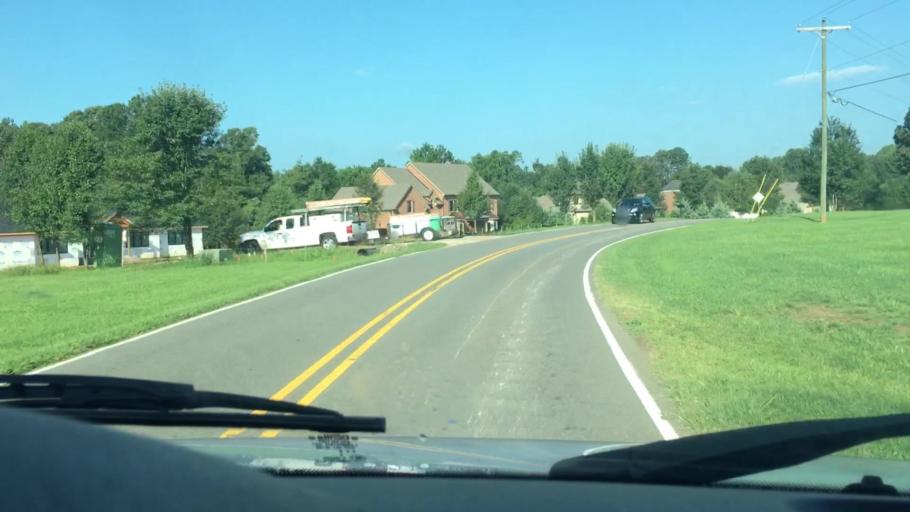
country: US
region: North Carolina
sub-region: Mecklenburg County
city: Huntersville
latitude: 35.4339
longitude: -80.8052
